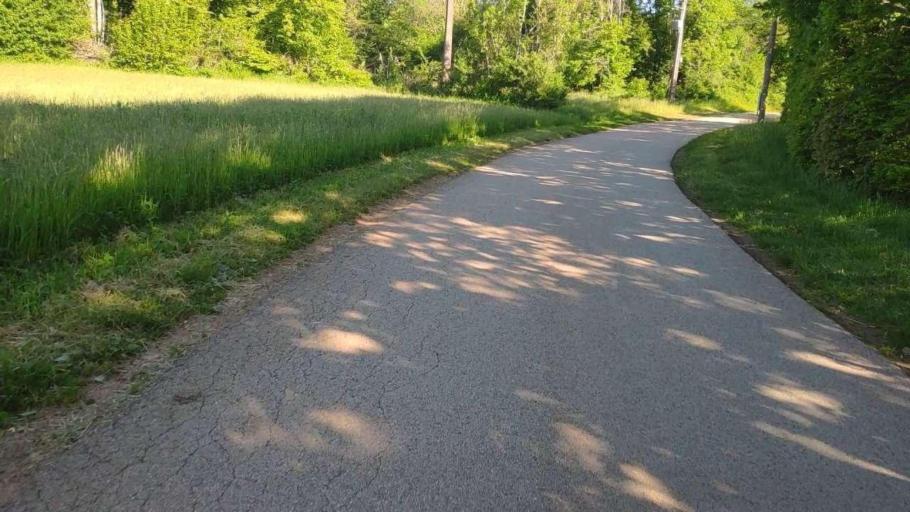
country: FR
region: Franche-Comte
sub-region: Departement du Jura
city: Perrigny
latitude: 46.6882
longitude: 5.6375
